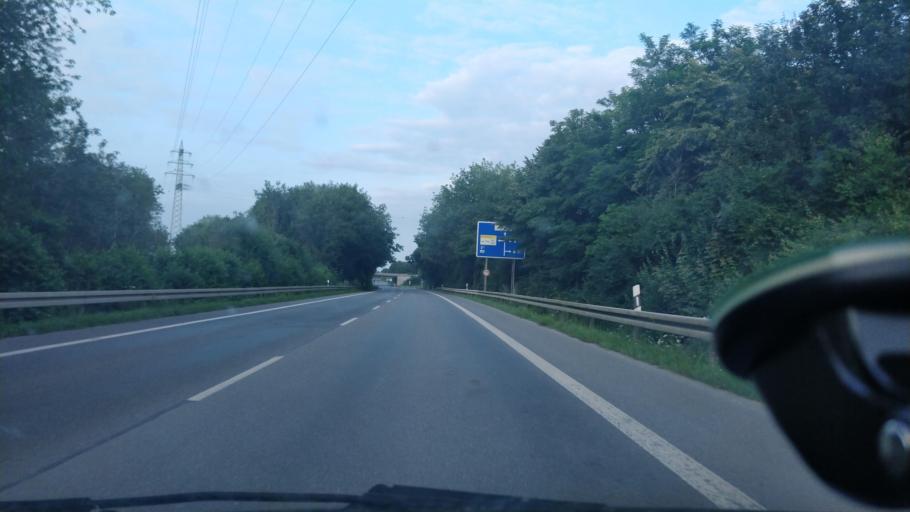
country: DE
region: North Rhine-Westphalia
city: Rheinberg
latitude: 51.5299
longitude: 6.5727
